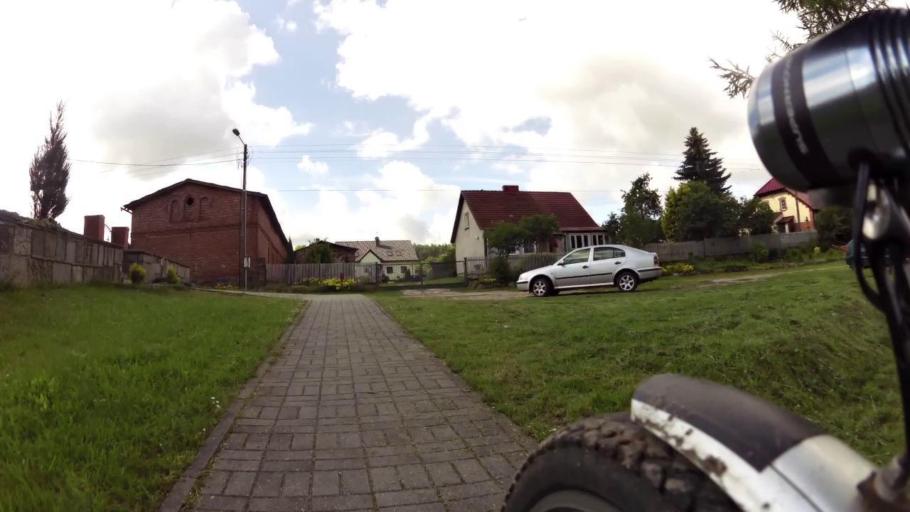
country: PL
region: West Pomeranian Voivodeship
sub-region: Powiat swidwinski
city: Rabino
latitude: 53.7574
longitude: 15.9138
